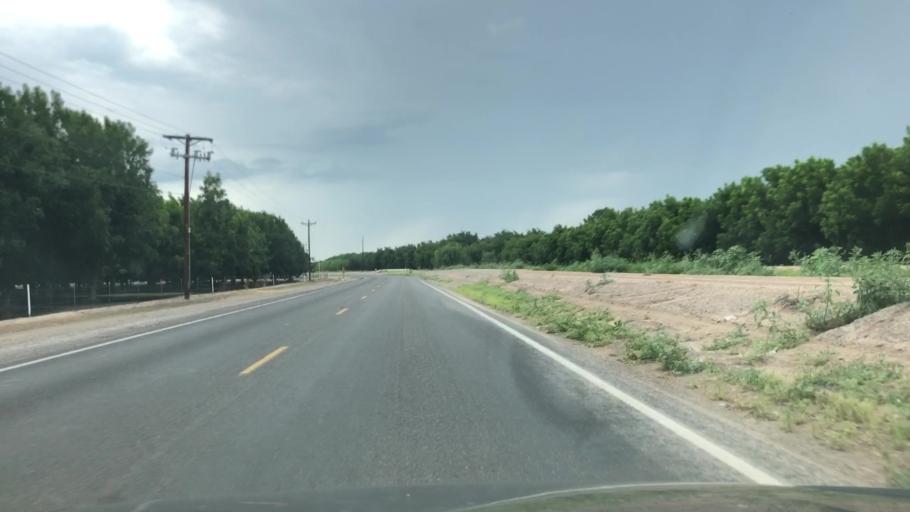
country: US
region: New Mexico
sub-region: Dona Ana County
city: La Union
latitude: 31.9903
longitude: -106.6510
